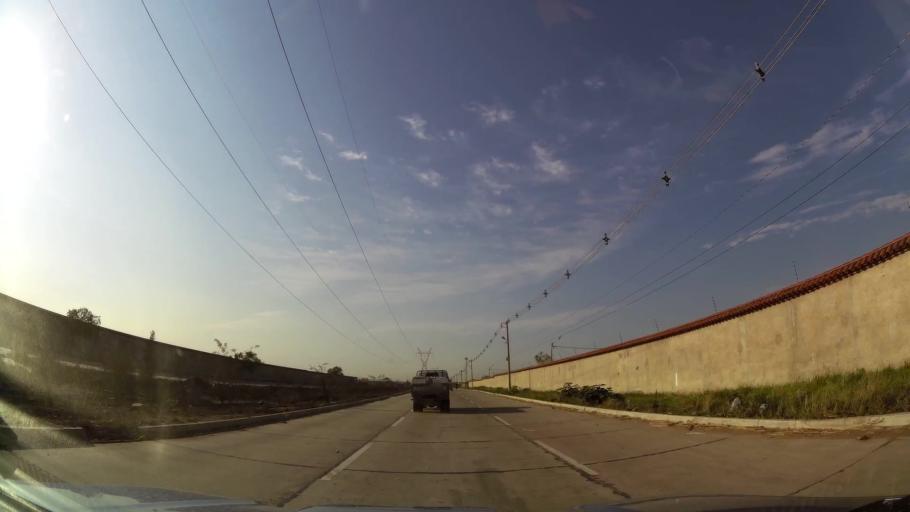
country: BO
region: Santa Cruz
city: Santa Cruz de la Sierra
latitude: -17.6813
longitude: -63.1519
